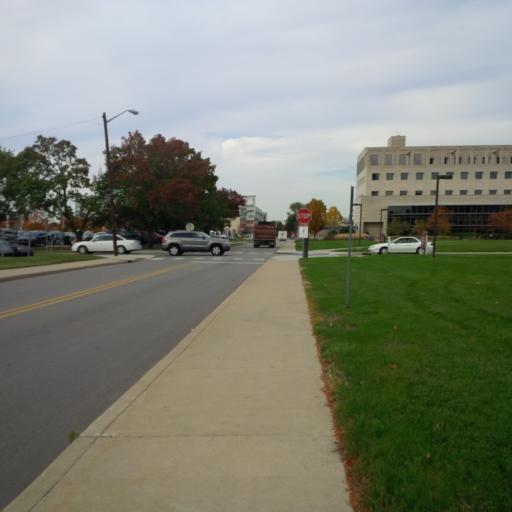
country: US
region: Indiana
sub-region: Marion County
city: Indianapolis
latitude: 39.7725
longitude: -86.1685
